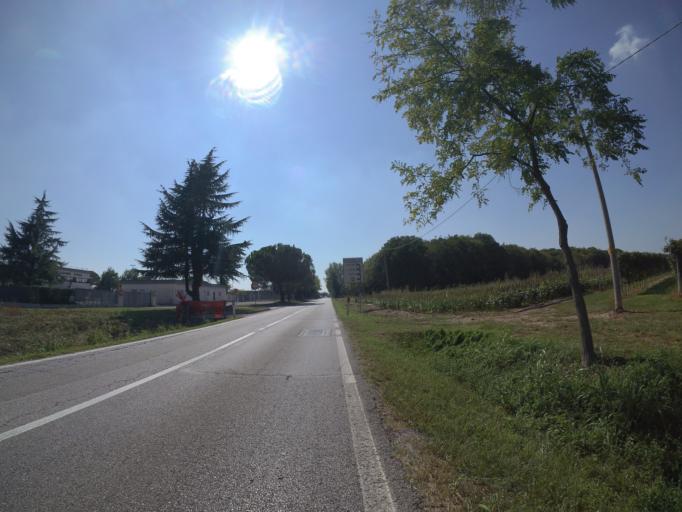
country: IT
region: Friuli Venezia Giulia
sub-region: Provincia di Udine
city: Codroipo
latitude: 45.9762
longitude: 12.9896
